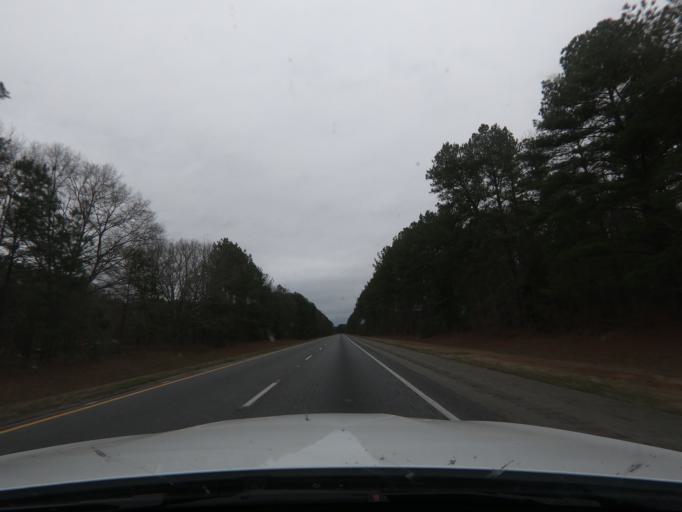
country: US
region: Georgia
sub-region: Troup County
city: La Grange
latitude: 32.9761
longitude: -84.9524
